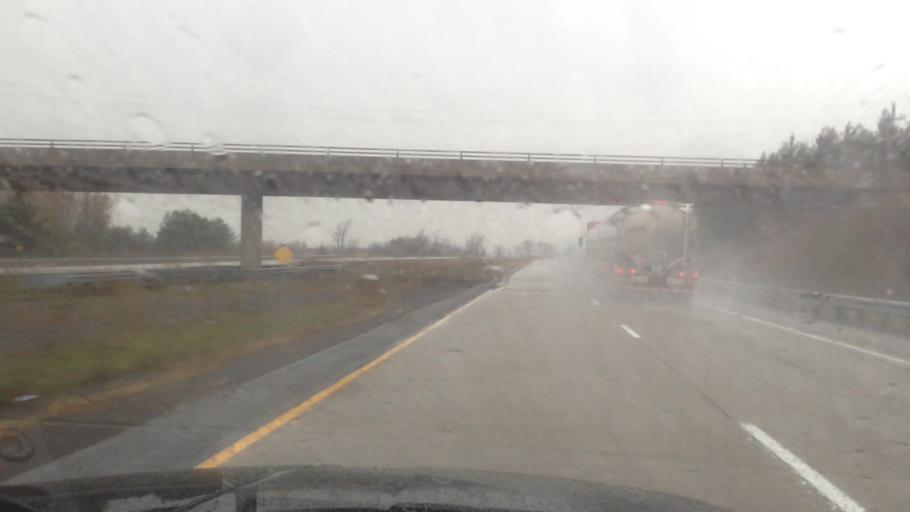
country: CA
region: Ontario
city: Hawkesbury
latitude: 45.4074
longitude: -74.7711
